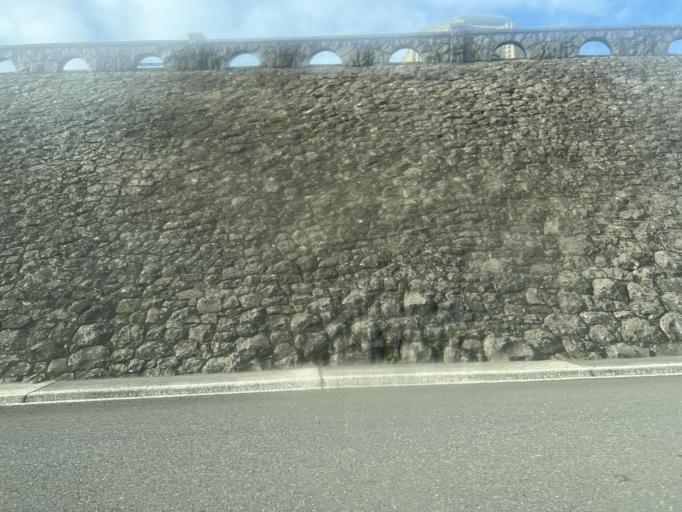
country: US
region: Washington
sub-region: Clark County
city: Washougal
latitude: 45.5394
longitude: -122.2440
